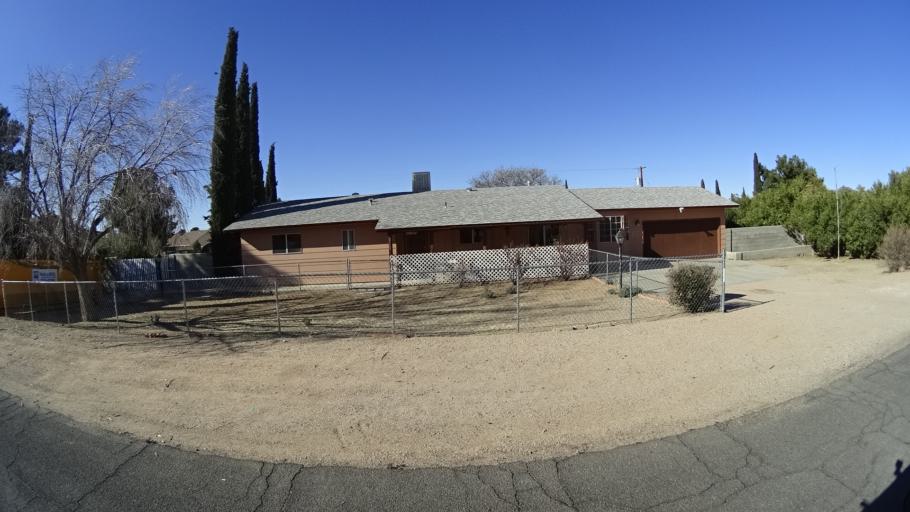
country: US
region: Arizona
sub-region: Mohave County
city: Kingman
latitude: 35.2068
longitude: -114.0068
